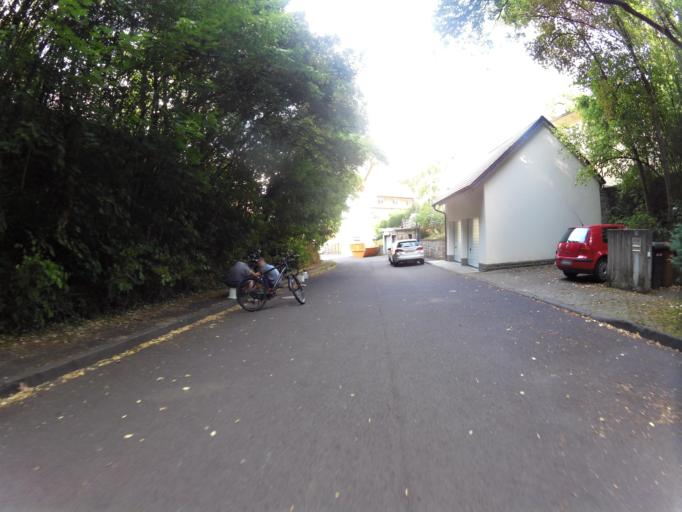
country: DE
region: Bavaria
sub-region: Regierungsbezirk Unterfranken
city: Ochsenfurt
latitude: 49.6582
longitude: 10.0597
